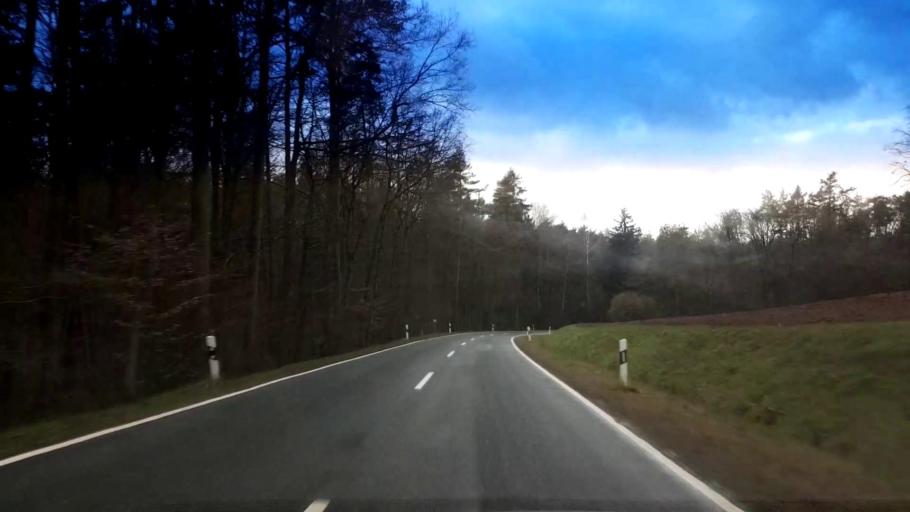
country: DE
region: Bavaria
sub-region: Upper Franconia
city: Lauter
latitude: 49.9640
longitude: 10.7655
